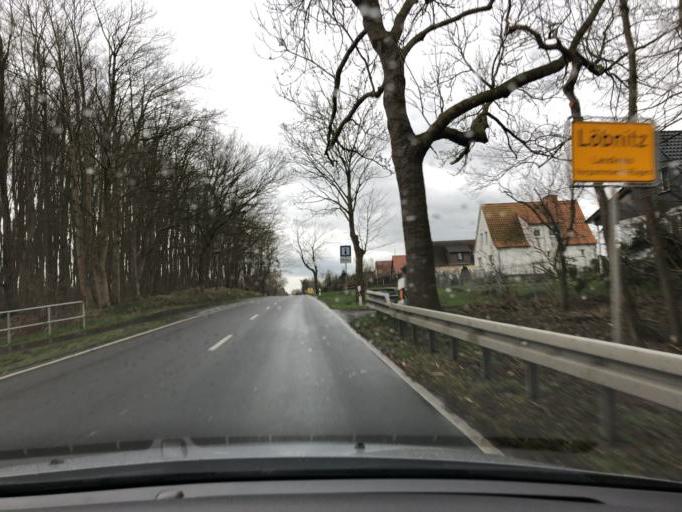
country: DE
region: Mecklenburg-Vorpommern
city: Barth
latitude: 54.2996
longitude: 12.7188
